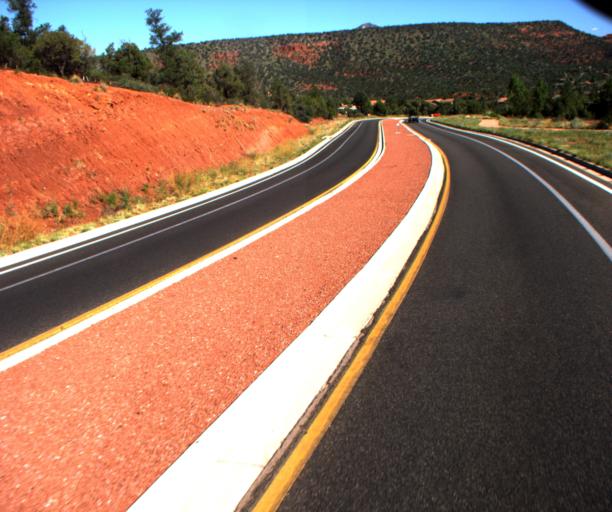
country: US
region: Arizona
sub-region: Coconino County
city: Sedona
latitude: 34.8346
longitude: -111.7765
